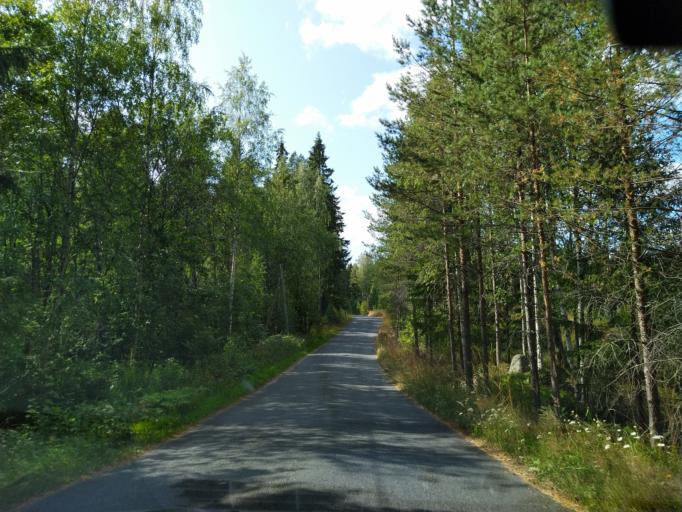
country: FI
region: Uusimaa
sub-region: Helsinki
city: Karkkila
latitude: 60.7198
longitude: 24.1804
